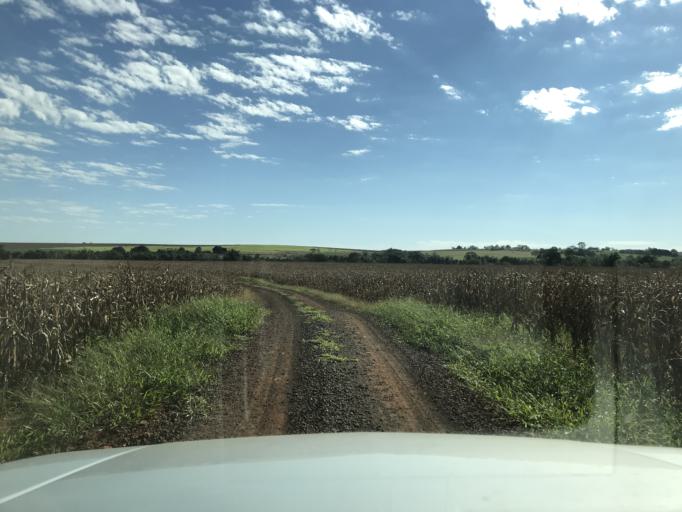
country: BR
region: Parana
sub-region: Ipora
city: Ipora
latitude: -24.1552
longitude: -53.7431
